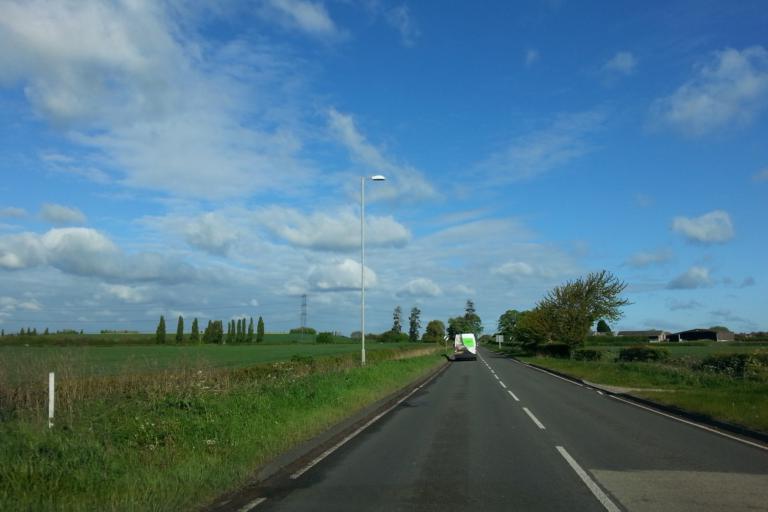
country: GB
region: England
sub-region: Nottinghamshire
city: Cotgrave
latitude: 52.9195
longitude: -1.0127
